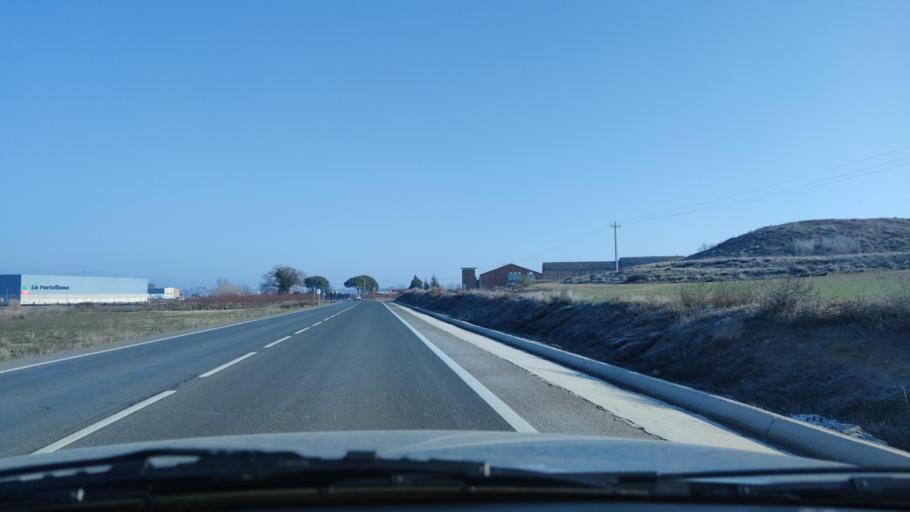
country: ES
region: Catalonia
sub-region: Provincia de Lleida
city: Albesa
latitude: 41.7339
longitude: 0.6409
